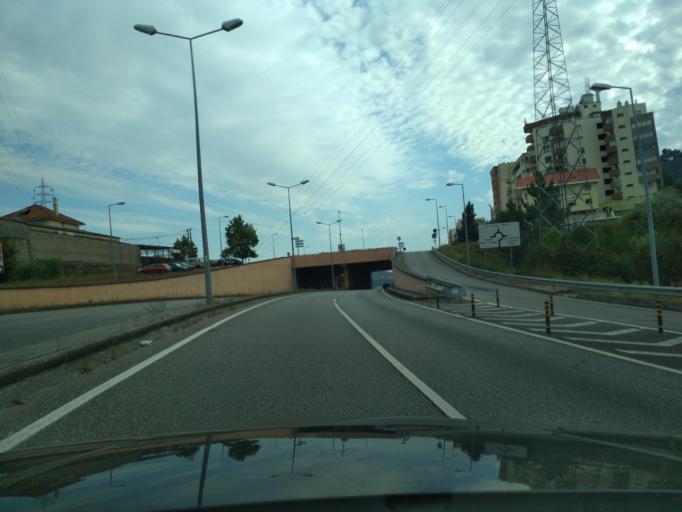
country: PT
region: Coimbra
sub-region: Coimbra
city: Coimbra
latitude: 40.2157
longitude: -8.3947
